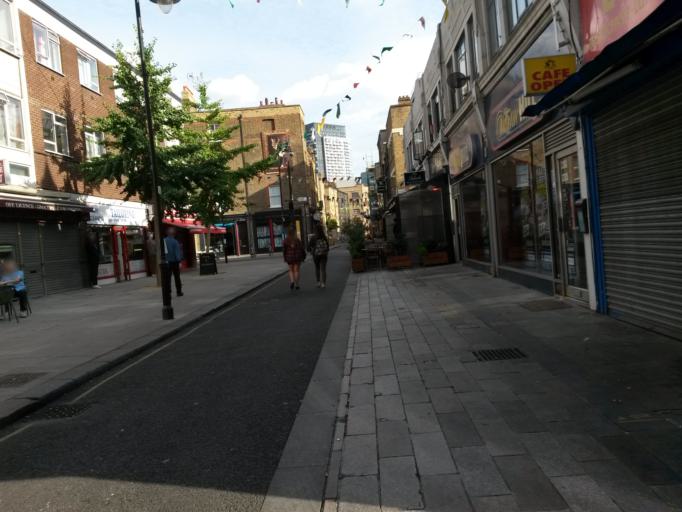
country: GB
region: England
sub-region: Greater London
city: Barbican
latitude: 51.5241
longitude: -0.0936
